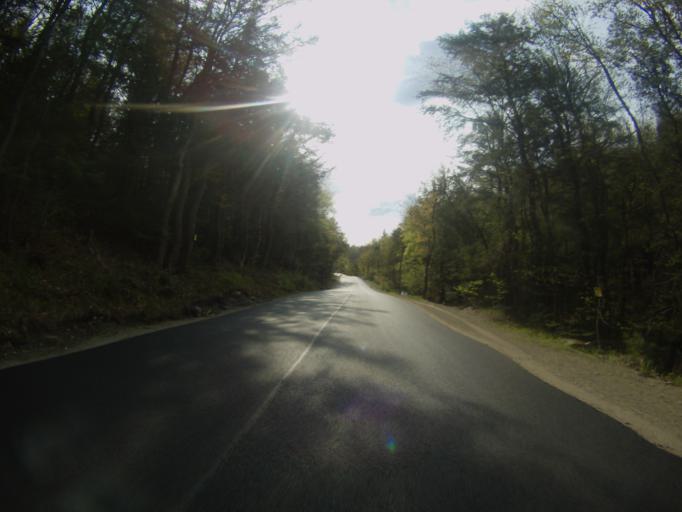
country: US
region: New York
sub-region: Warren County
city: Warrensburg
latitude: 43.8414
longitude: -73.7852
